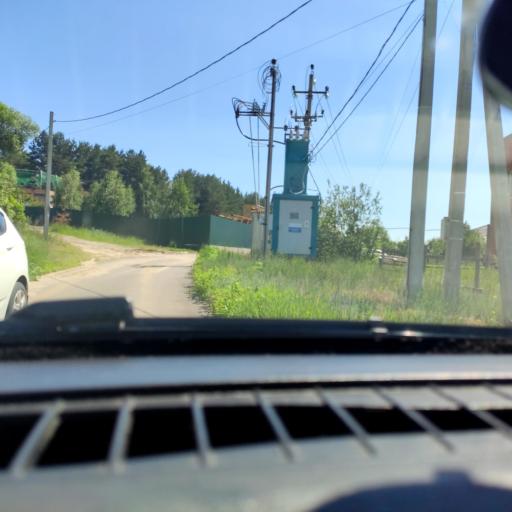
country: RU
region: Voronezj
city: Podgornoye
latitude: 51.7932
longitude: 39.1354
